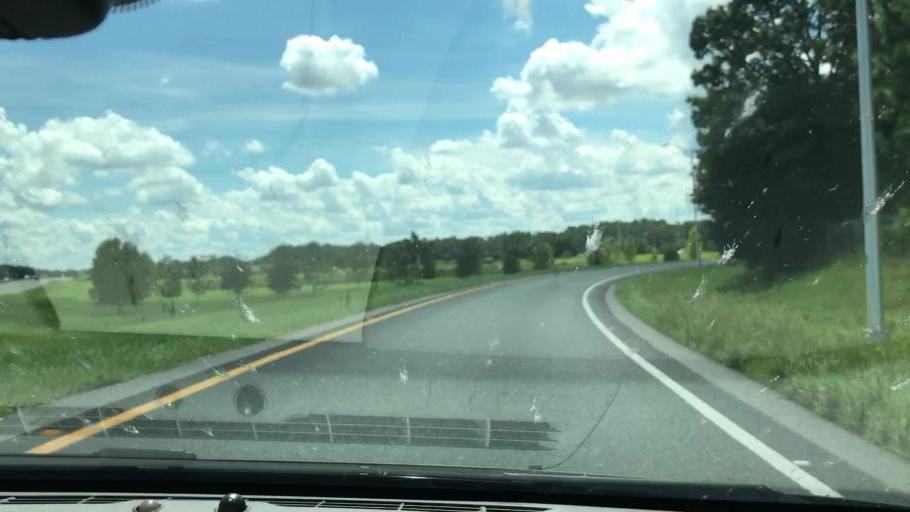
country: US
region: Florida
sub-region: Marion County
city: Ocala
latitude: 29.2714
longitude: -82.1955
